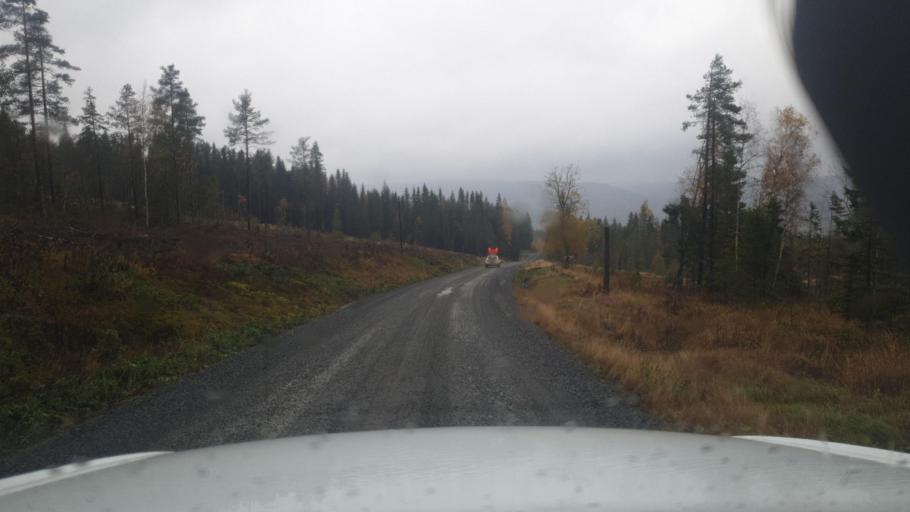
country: SE
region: Vaermland
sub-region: Torsby Kommun
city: Torsby
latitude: 60.1767
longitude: 12.6457
